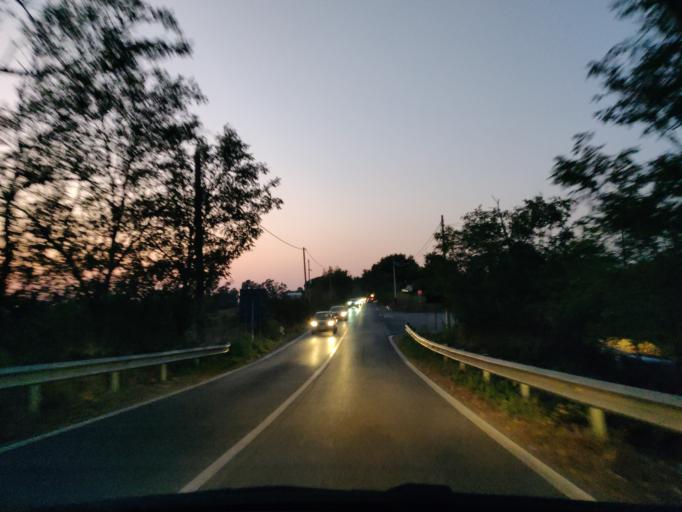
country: IT
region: Latium
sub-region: Citta metropolitana di Roma Capitale
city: Npp 23 (Parco Leonardo)
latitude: 41.8360
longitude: 12.2808
